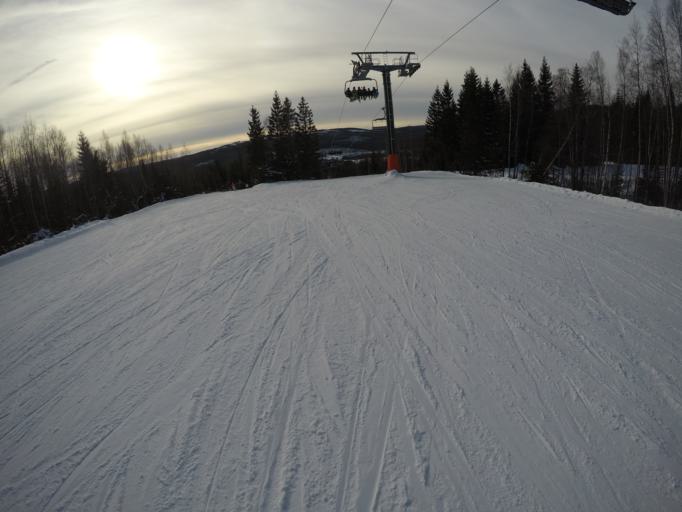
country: SE
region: Dalarna
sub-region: Borlange Kommun
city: Borlaenge
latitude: 60.3788
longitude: 15.4116
